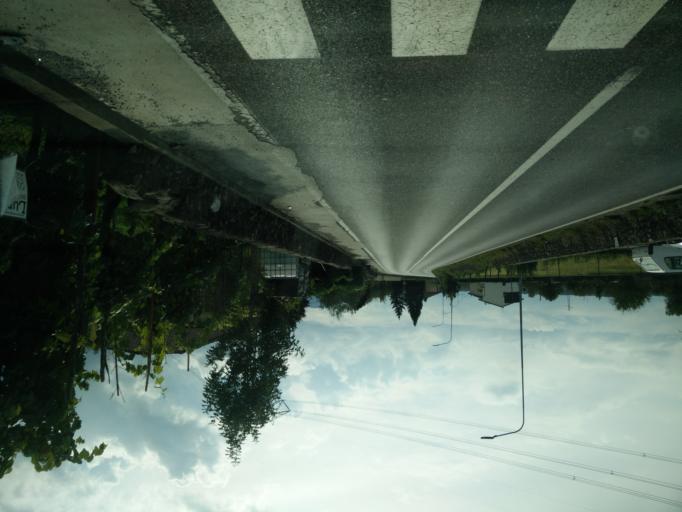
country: IT
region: Tuscany
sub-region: Provincia di Massa-Carrara
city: Pontremoli
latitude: 44.3564
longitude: 9.9032
